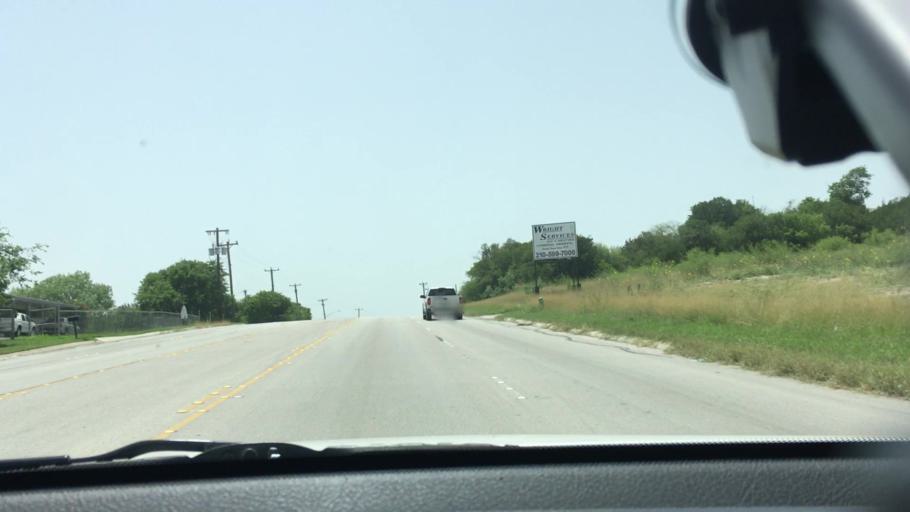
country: US
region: Texas
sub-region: Bexar County
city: Live Oak
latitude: 29.5662
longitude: -98.3540
